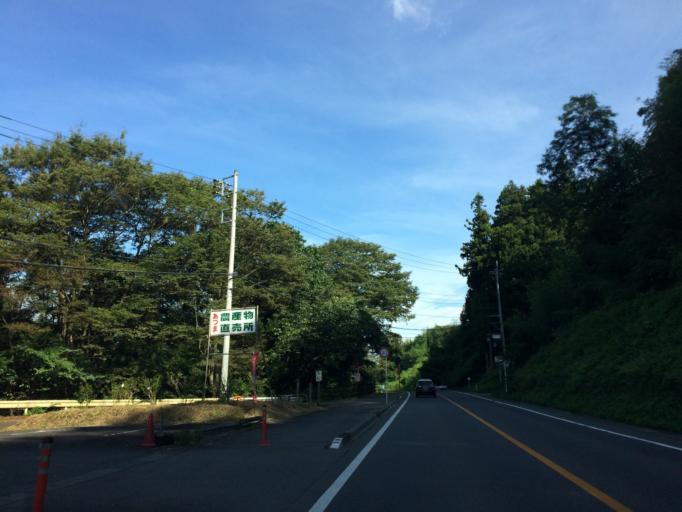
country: JP
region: Gunma
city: Nakanojomachi
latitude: 36.5546
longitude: 138.8974
